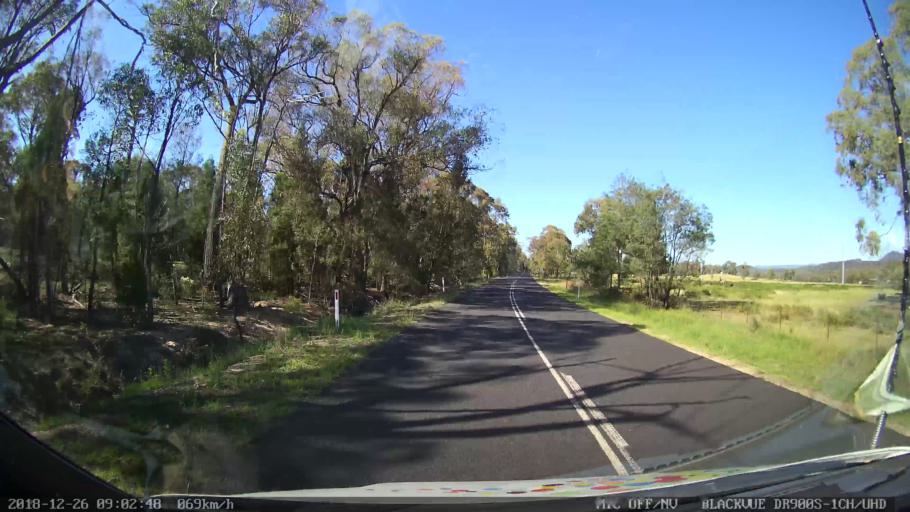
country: AU
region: New South Wales
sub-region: Mid-Western Regional
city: Kandos
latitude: -32.6565
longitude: 150.0173
